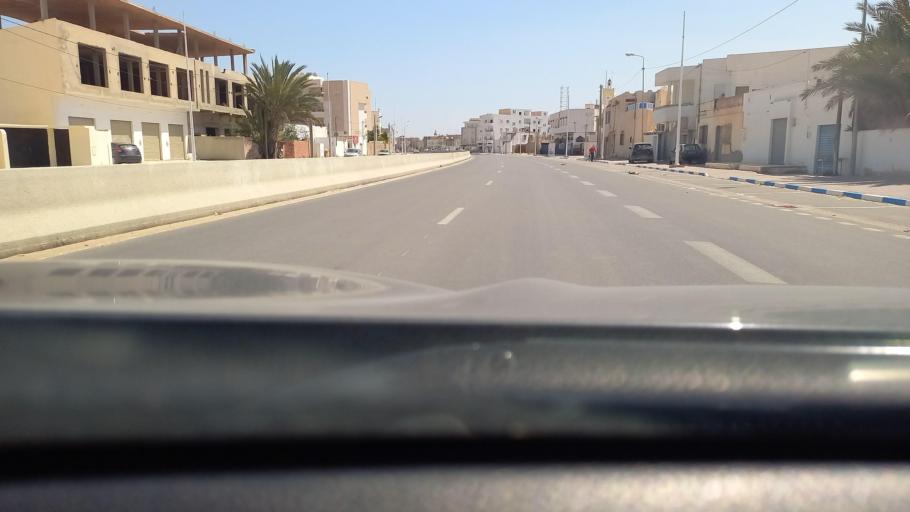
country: TN
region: Safaqis
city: Sfax
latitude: 34.7423
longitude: 10.7243
